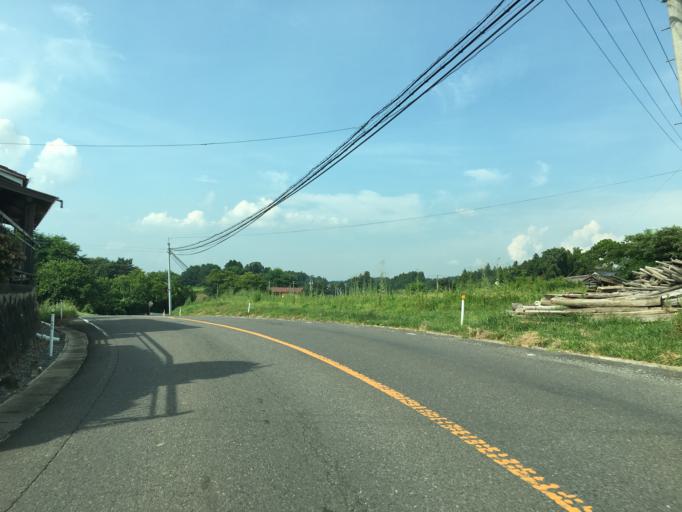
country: JP
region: Fukushima
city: Koriyama
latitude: 37.3472
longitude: 140.4125
